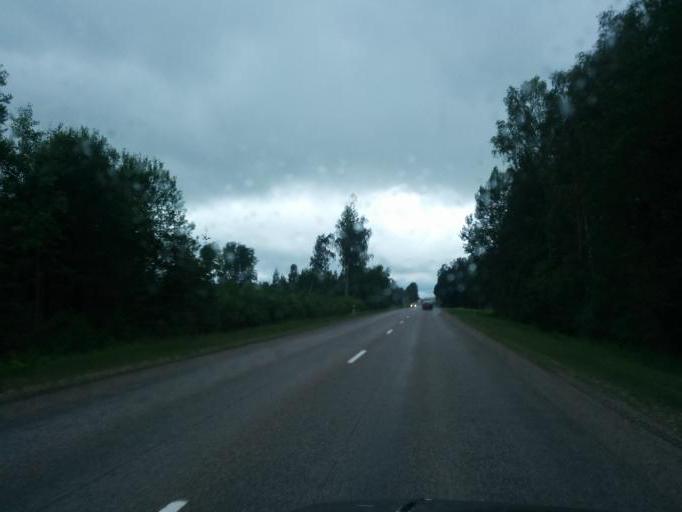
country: LV
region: Beverina
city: Murmuiza
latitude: 57.4890
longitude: 25.5818
